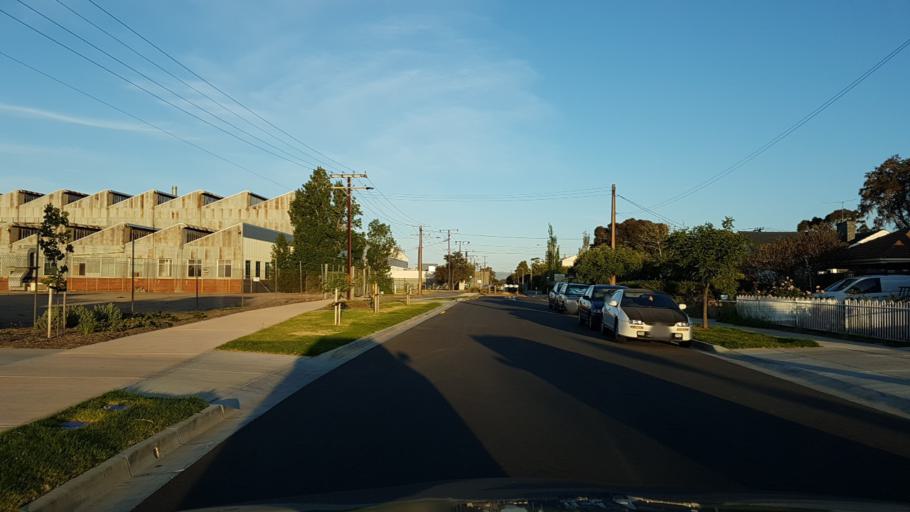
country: AU
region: South Australia
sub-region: Port Adelaide Enfield
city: Alberton
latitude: -34.8631
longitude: 138.5333
